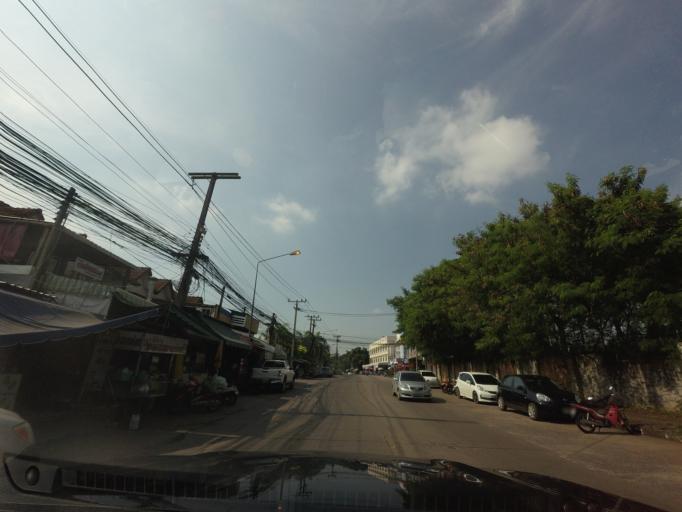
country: TH
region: Khon Kaen
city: Khon Kaen
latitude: 16.4237
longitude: 102.8503
